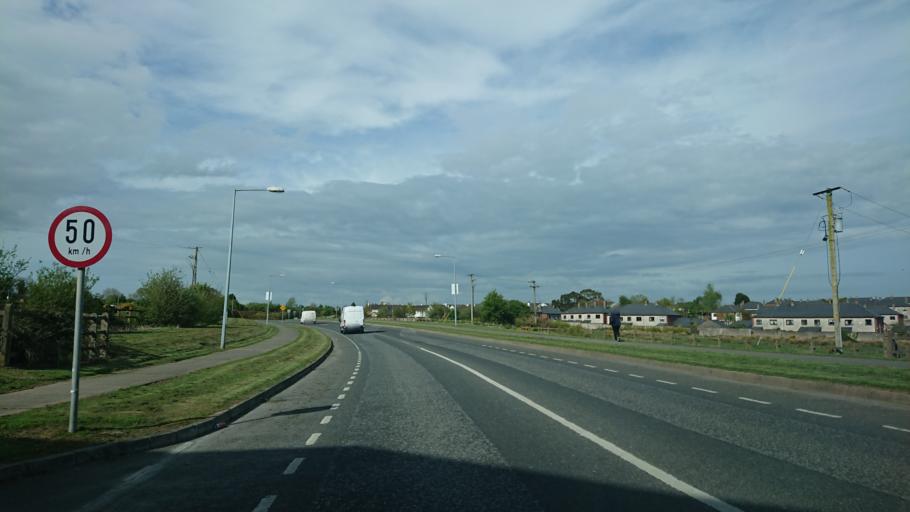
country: IE
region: Munster
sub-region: Waterford
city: Waterford
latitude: 52.2628
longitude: -7.1422
